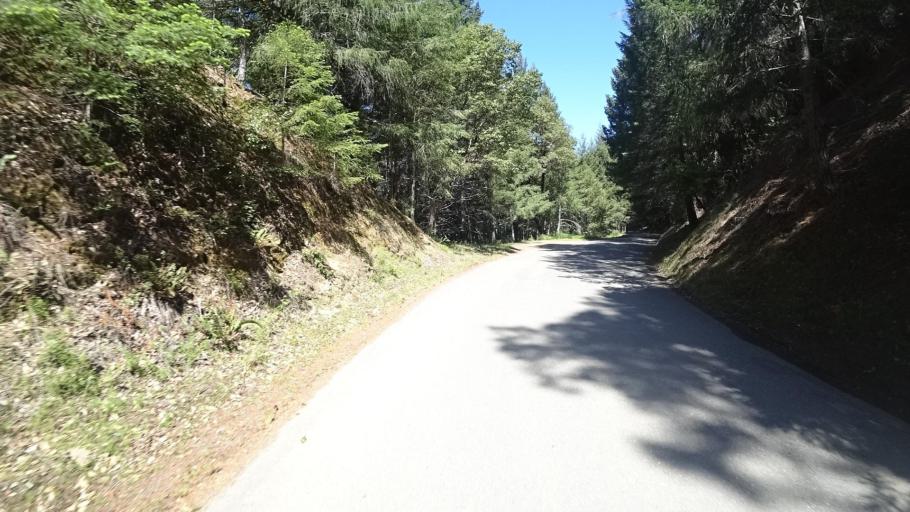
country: US
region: California
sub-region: Humboldt County
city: Redway
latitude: 40.1030
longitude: -123.9530
